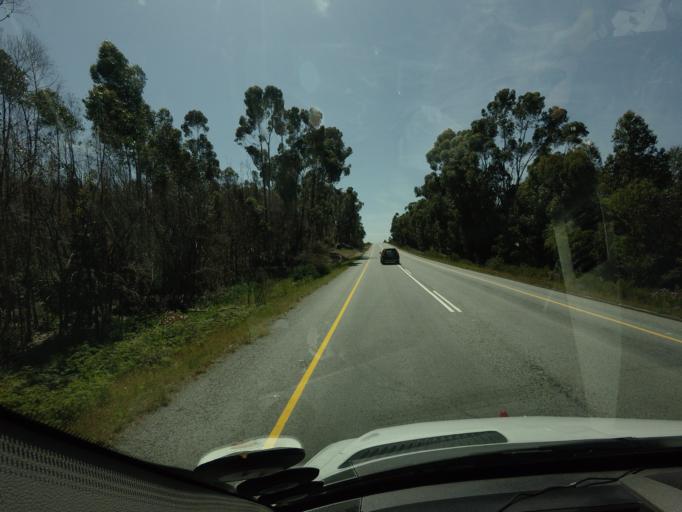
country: ZA
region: Western Cape
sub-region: Overberg District Municipality
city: Hermanus
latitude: -34.3198
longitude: 19.1147
